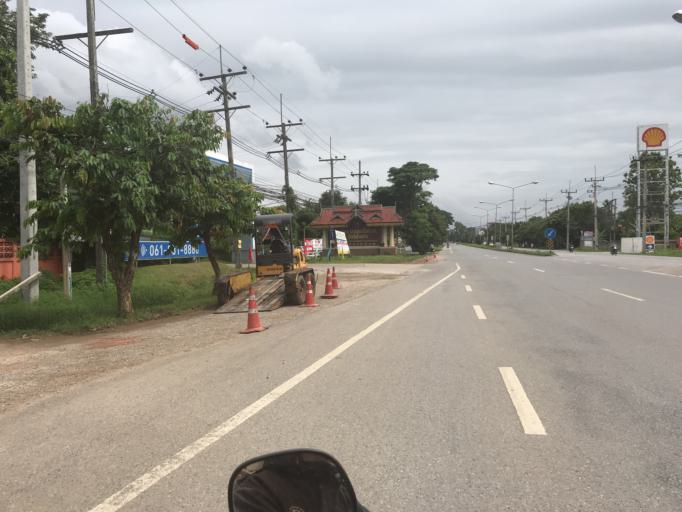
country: TH
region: Chiang Rai
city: Chiang Rai
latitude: 19.9456
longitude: 99.8473
